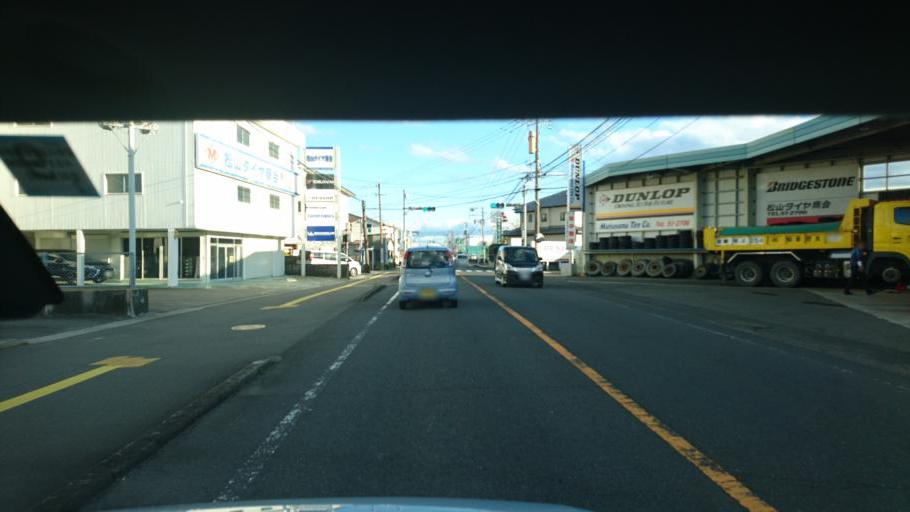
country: JP
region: Miyazaki
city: Miyazaki-shi
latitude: 31.8909
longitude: 131.4211
